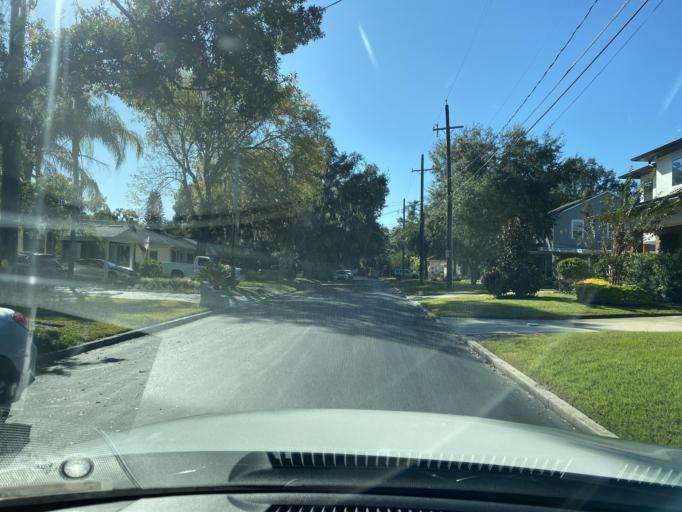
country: US
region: Florida
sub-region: Orange County
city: Orlando
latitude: 28.5615
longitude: -81.3857
